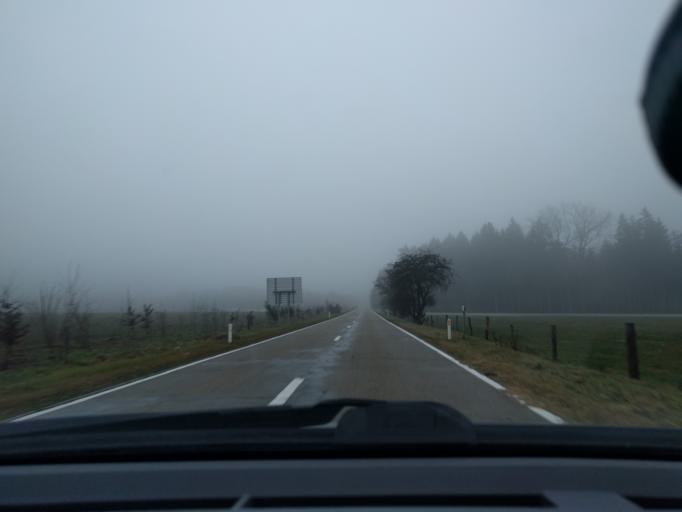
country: BE
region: Wallonia
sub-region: Province du Luxembourg
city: Gouvy
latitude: 50.2043
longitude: 5.9206
